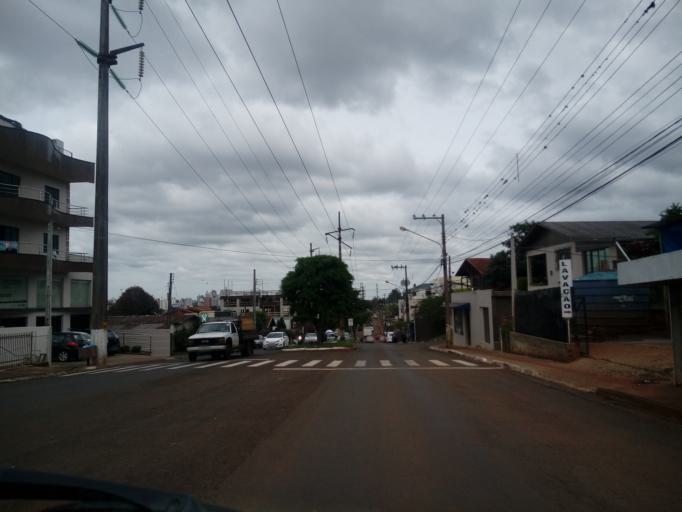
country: BR
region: Santa Catarina
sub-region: Chapeco
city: Chapeco
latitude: -27.0779
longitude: -52.6127
